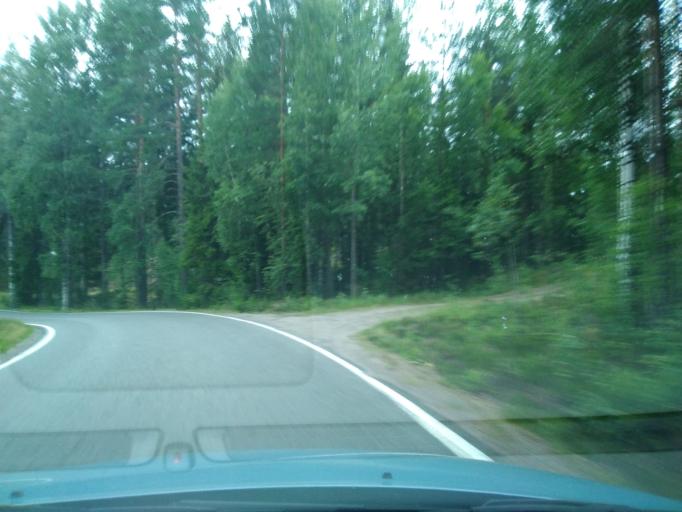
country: FI
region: Uusimaa
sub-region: Helsinki
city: Kaerkoelae
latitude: 60.7778
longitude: 24.0724
